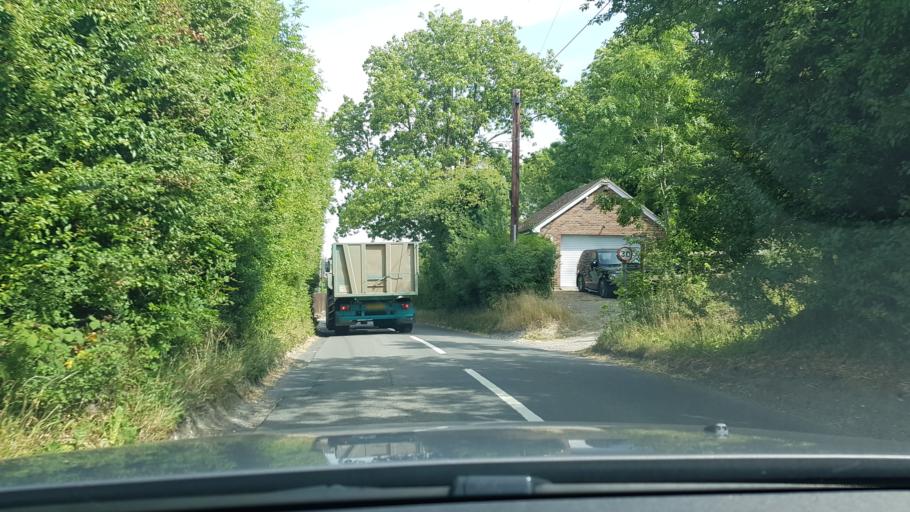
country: GB
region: England
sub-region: West Berkshire
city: Lambourn
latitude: 51.5044
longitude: -1.5352
